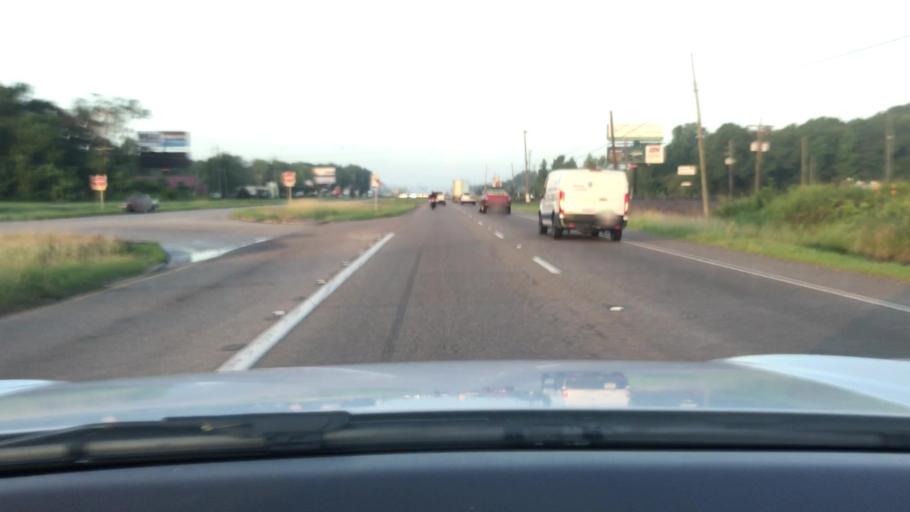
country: US
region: Louisiana
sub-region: West Baton Rouge Parish
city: Port Allen
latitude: 30.4187
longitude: -91.2215
